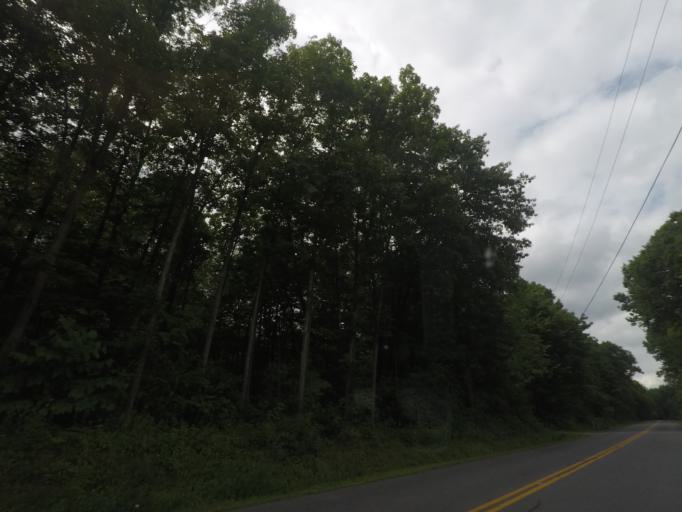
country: US
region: New York
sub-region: Saratoga County
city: Stillwater
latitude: 42.9920
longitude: -73.6908
